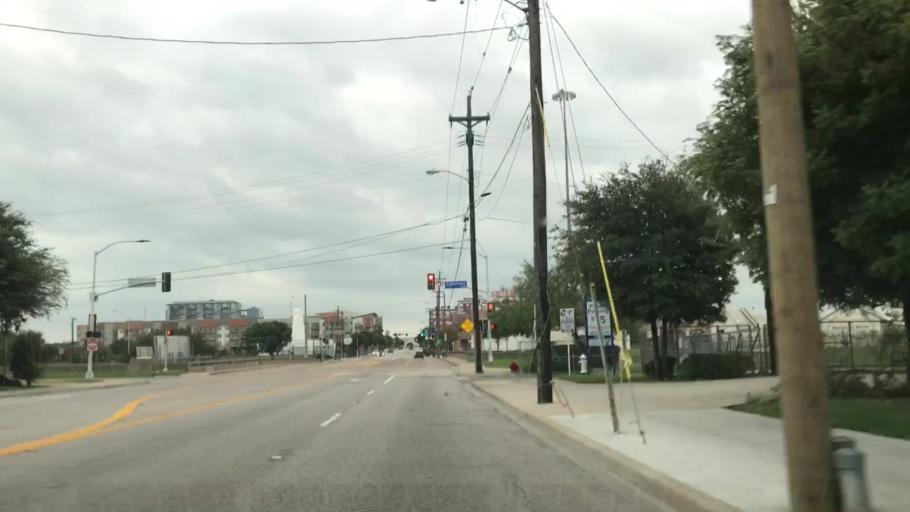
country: US
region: Texas
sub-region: Dallas County
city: Dallas
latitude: 32.7718
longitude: -96.8014
